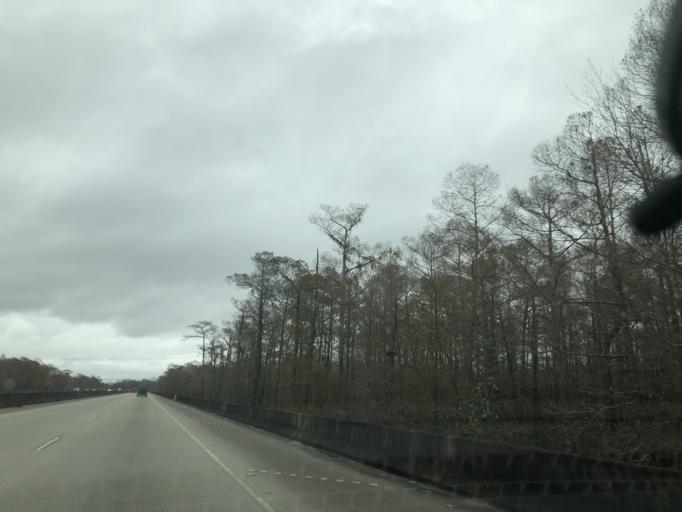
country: US
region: Louisiana
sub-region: Saint Charles Parish
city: Destrehan
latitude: 29.9648
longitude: -90.3455
